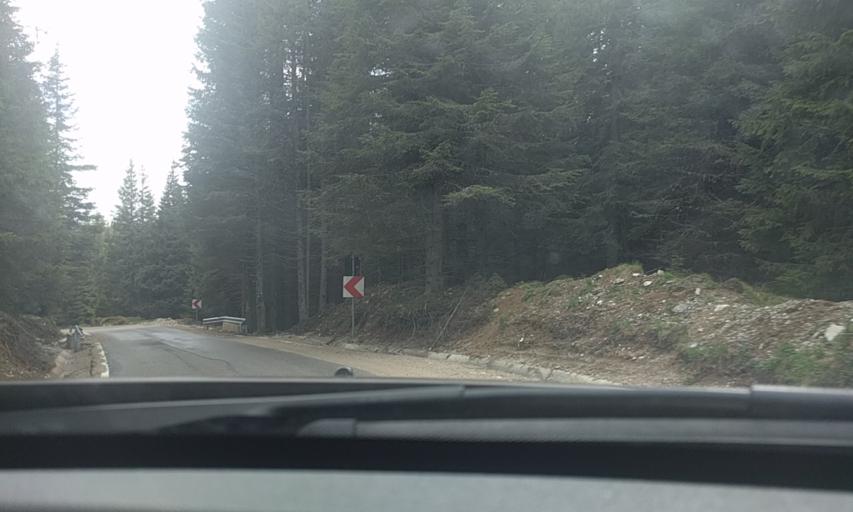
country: RO
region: Prahova
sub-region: Oras Busteni
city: Busteni
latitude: 45.3896
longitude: 25.4391
